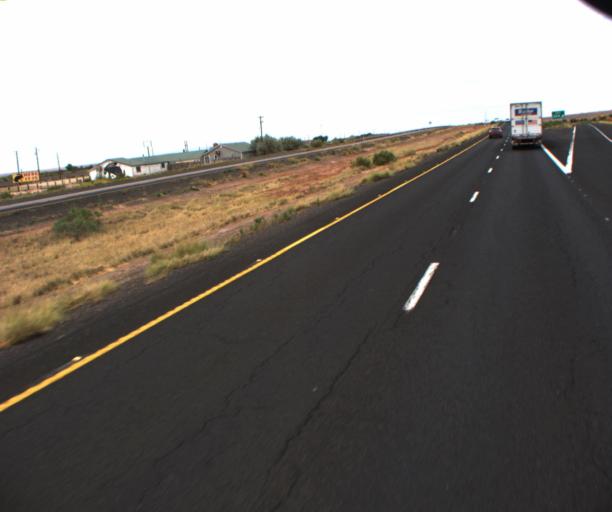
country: US
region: Arizona
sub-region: Navajo County
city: Joseph City
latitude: 34.9687
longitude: -110.4287
